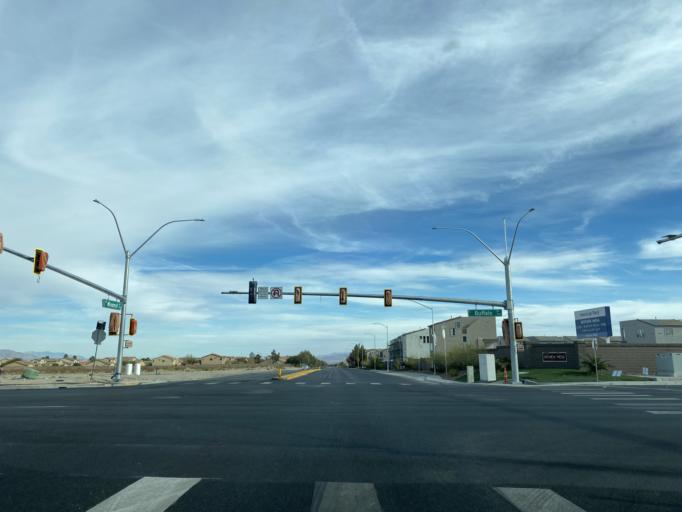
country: US
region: Nevada
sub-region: Clark County
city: Enterprise
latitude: 36.0410
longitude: -115.2615
